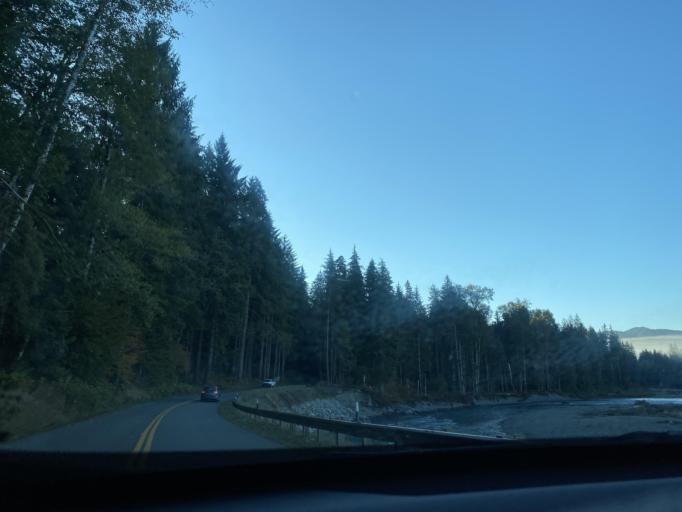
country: US
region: Washington
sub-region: Clallam County
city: Forks
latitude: 47.8173
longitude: -124.1121
